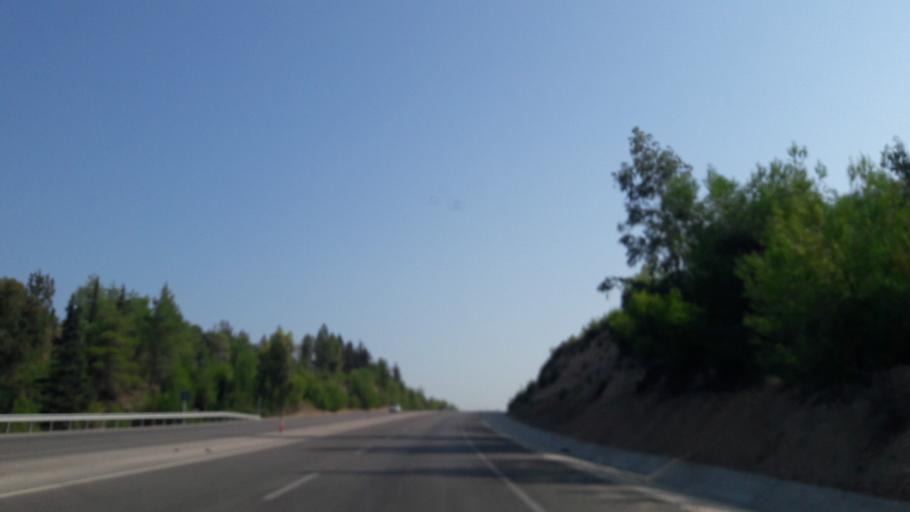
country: TR
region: Adana
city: Sagkaya
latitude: 37.1524
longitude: 35.5453
